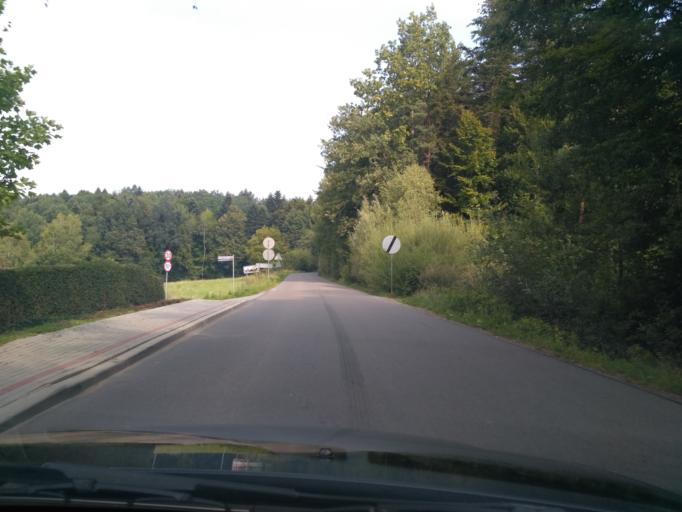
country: PL
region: Subcarpathian Voivodeship
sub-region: Powiat strzyzowski
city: Czudec
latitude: 49.9635
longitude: 21.8427
